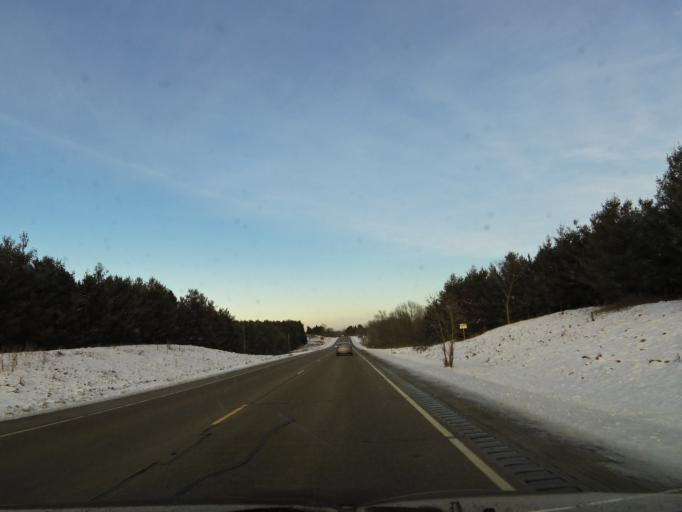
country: US
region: Minnesota
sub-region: Chisago County
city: Shafer
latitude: 45.3701
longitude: -92.7099
